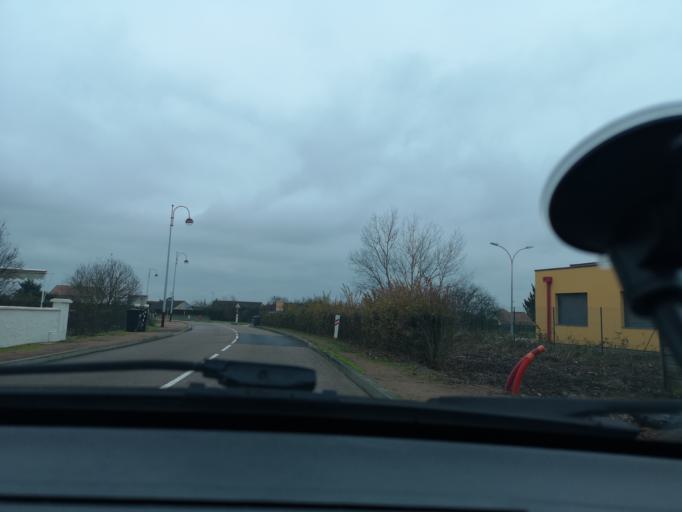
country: FR
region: Bourgogne
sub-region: Departement de Saone-et-Loire
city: Crissey
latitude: 46.8213
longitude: 4.8715
